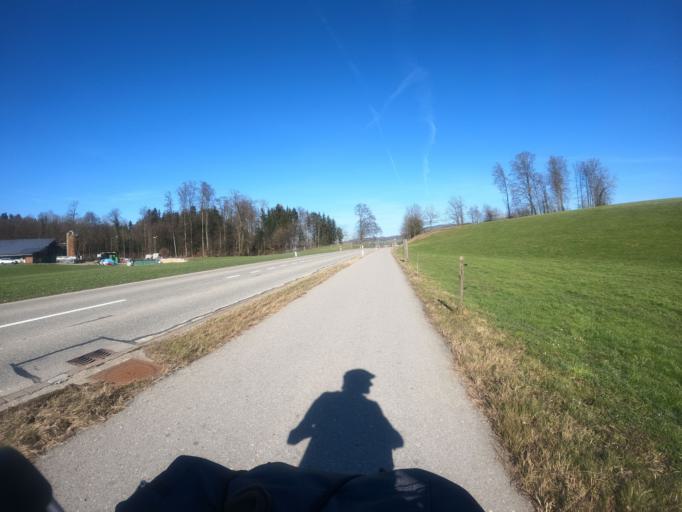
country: CH
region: Zurich
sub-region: Bezirk Affoltern
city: Mettmenstetten
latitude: 47.2383
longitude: 8.4513
